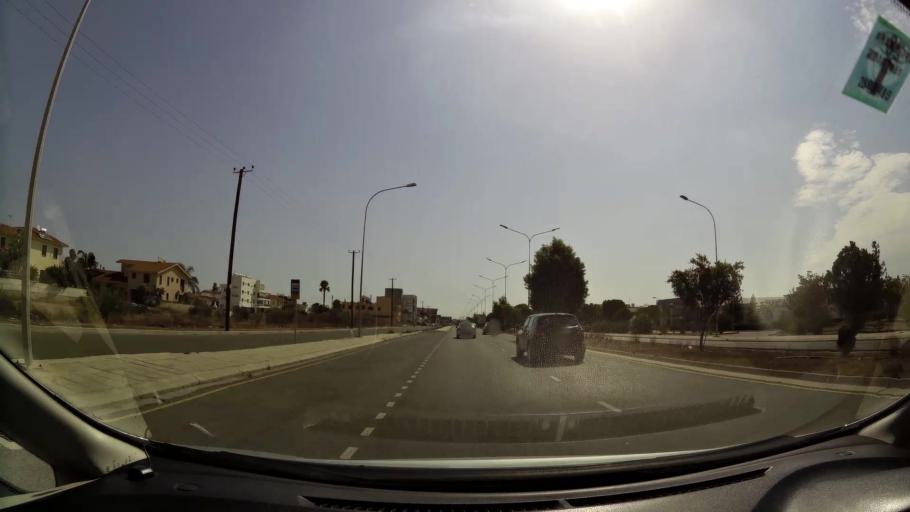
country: CY
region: Larnaka
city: Aradippou
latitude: 34.9396
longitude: 33.5868
